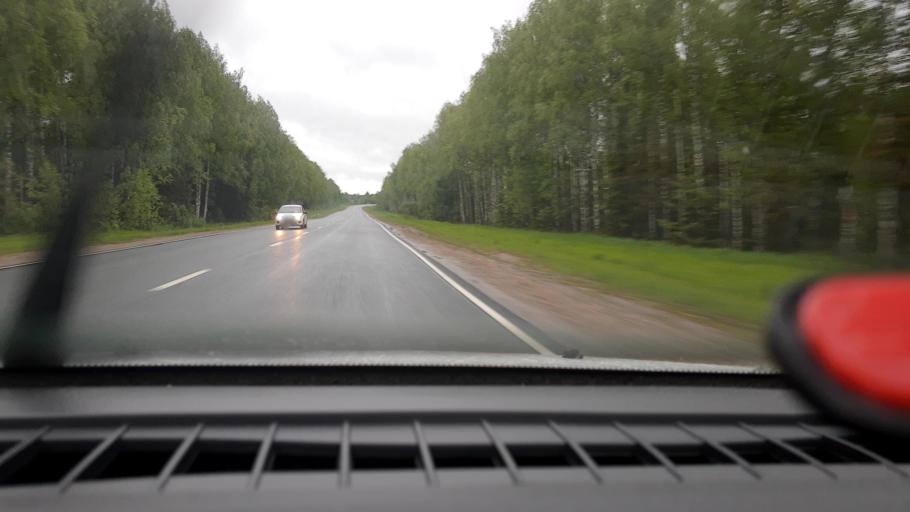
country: RU
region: Nizjnij Novgorod
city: Vladimirskoye
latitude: 56.9513
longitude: 45.0896
